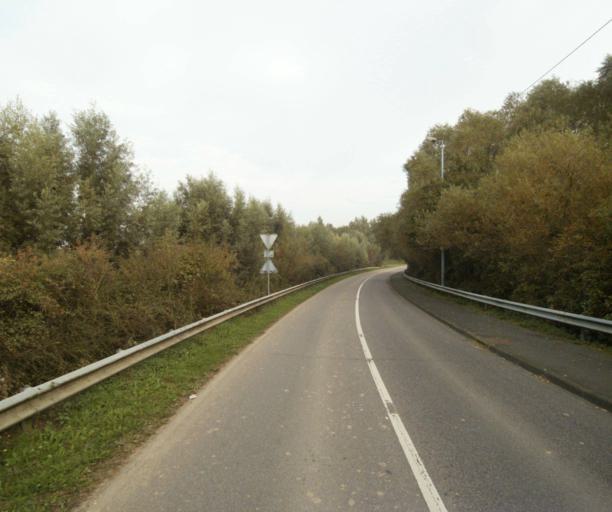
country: FR
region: Nord-Pas-de-Calais
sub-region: Departement du Nord
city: Seclin
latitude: 50.5377
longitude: 3.0277
